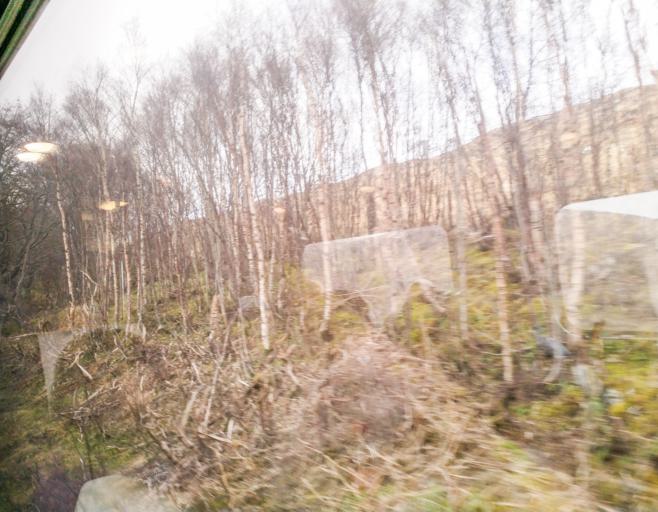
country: GB
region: Scotland
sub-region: Highland
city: Spean Bridge
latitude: 56.7830
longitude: -4.7326
